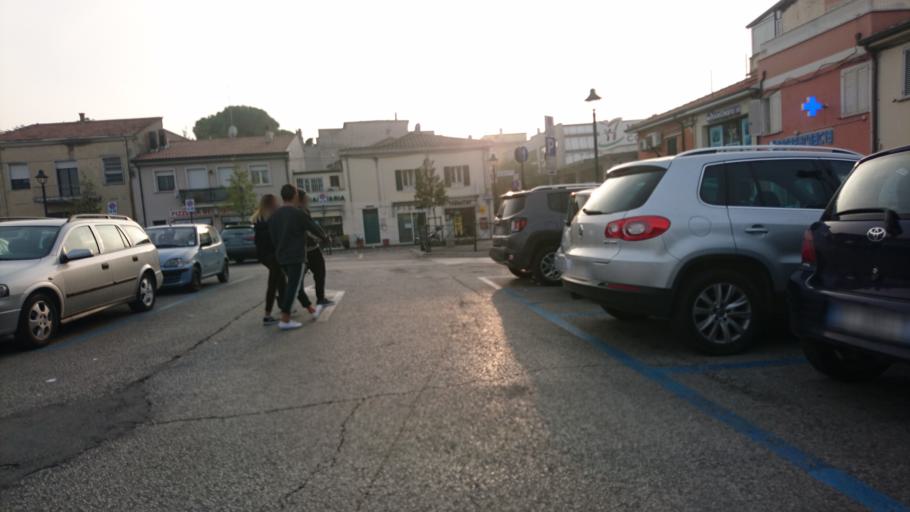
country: IT
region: Emilia-Romagna
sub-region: Provincia di Rimini
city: Rimini
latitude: 44.0597
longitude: 12.5728
